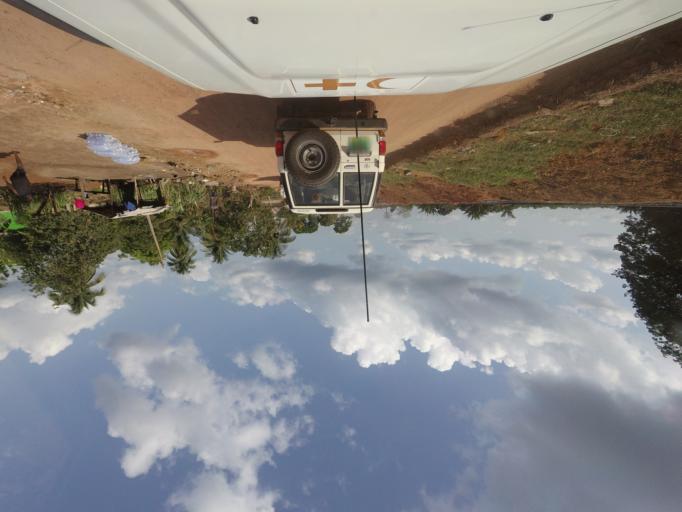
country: LR
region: Bong
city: Gbarnga
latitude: 7.0238
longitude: -9.5561
